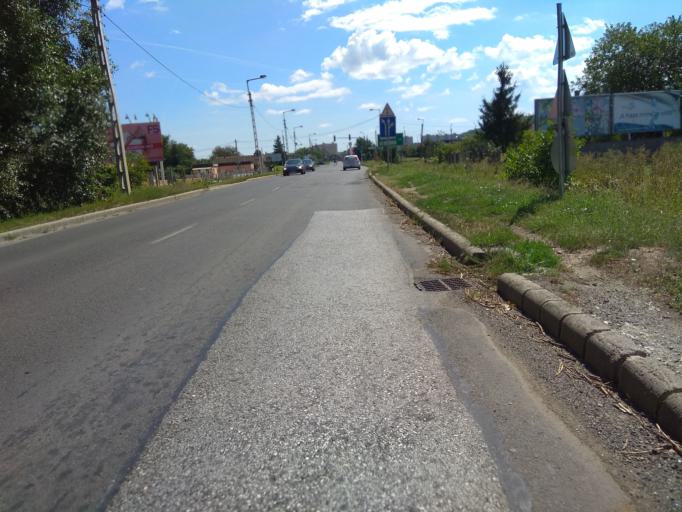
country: HU
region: Borsod-Abauj-Zemplen
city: Kazincbarcika
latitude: 48.2619
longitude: 20.6158
